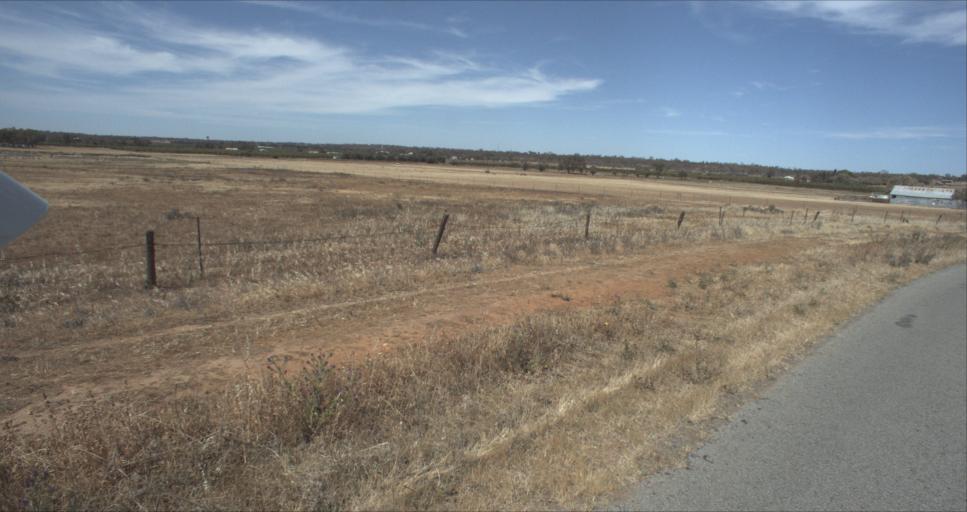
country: AU
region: New South Wales
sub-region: Leeton
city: Leeton
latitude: -34.5713
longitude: 146.4625
